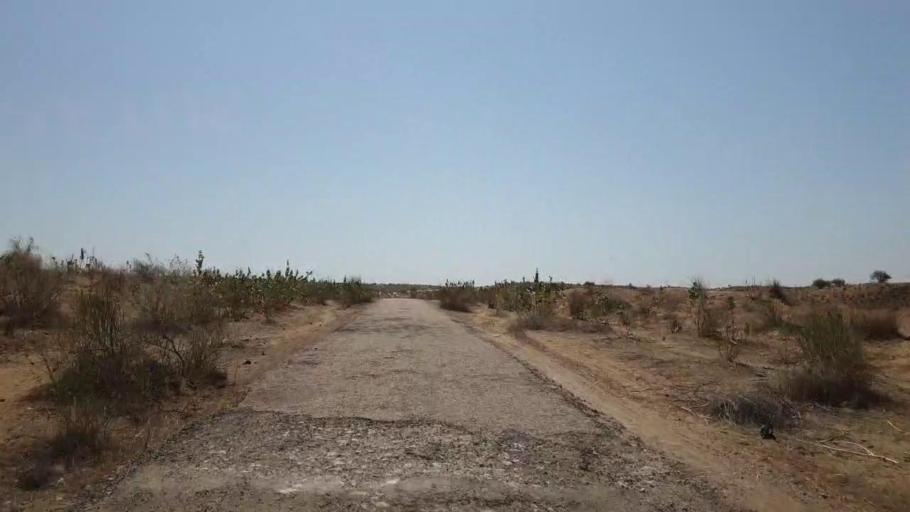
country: PK
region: Sindh
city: Nabisar
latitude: 25.1278
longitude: 69.9164
